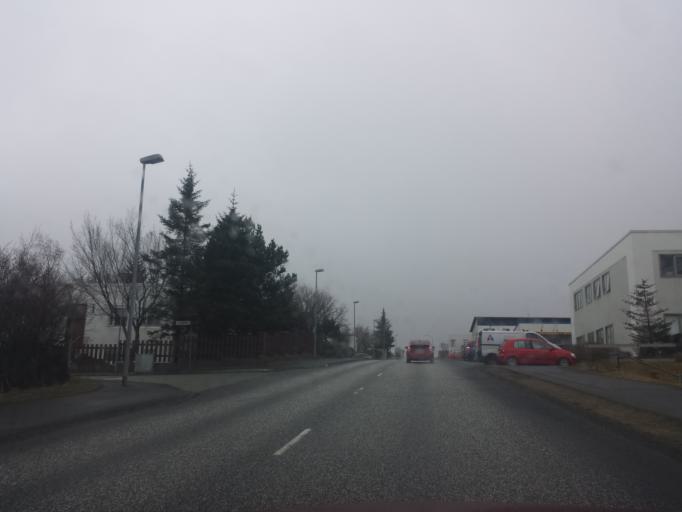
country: IS
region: Capital Region
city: Reykjavik
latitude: 64.1130
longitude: -21.8675
